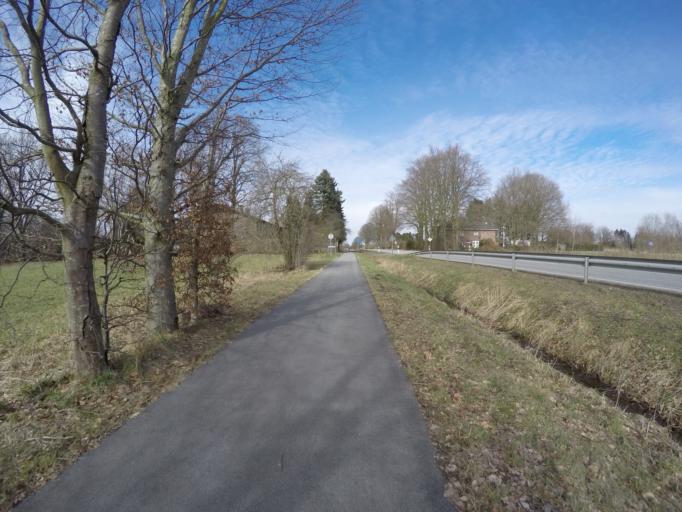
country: DE
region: Schleswig-Holstein
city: Langeln
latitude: 53.8044
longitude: 9.8785
